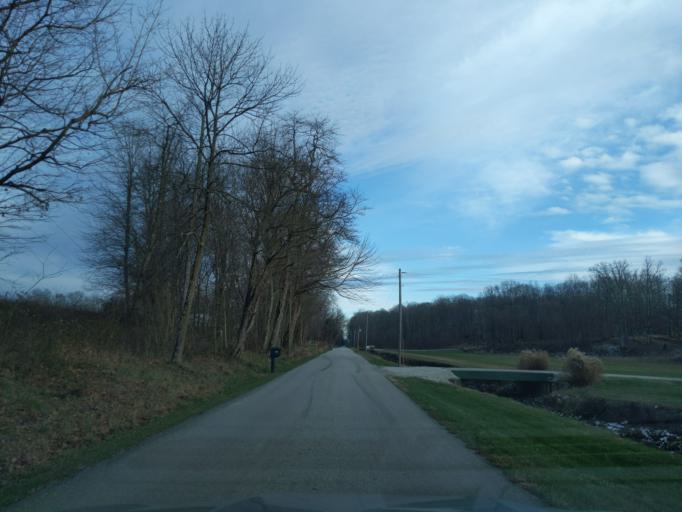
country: US
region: Indiana
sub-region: Decatur County
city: Westport
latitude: 39.2196
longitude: -85.5074
